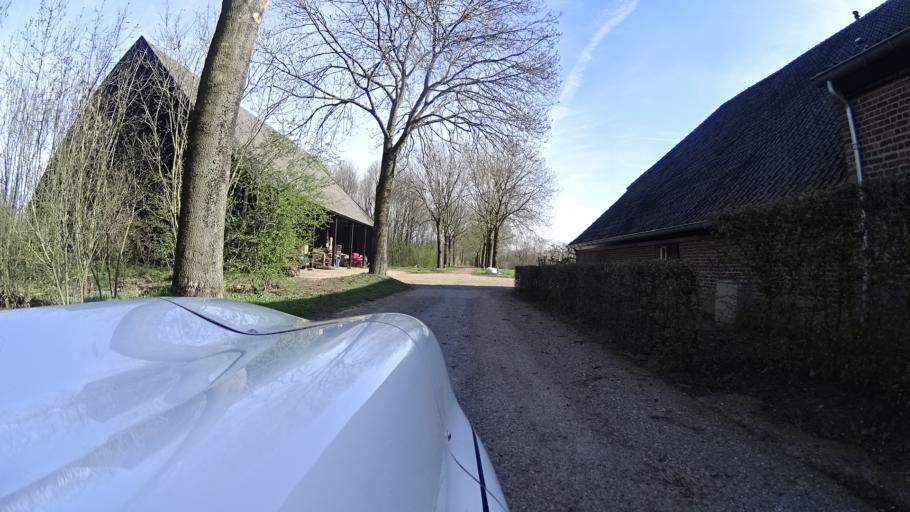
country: NL
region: North Brabant
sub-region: Gemeente Mill en Sint Hubert
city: Wilbertoord
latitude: 51.7147
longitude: 5.7799
